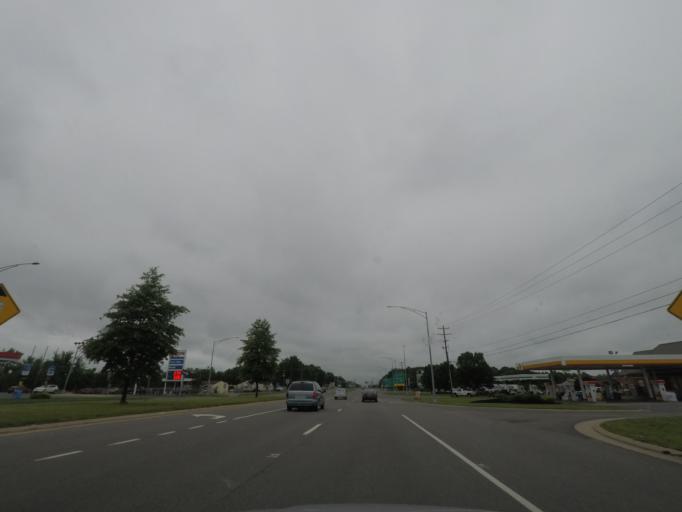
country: US
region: Virginia
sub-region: Fluvanna County
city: Palmyra
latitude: 37.9731
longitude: -78.2171
